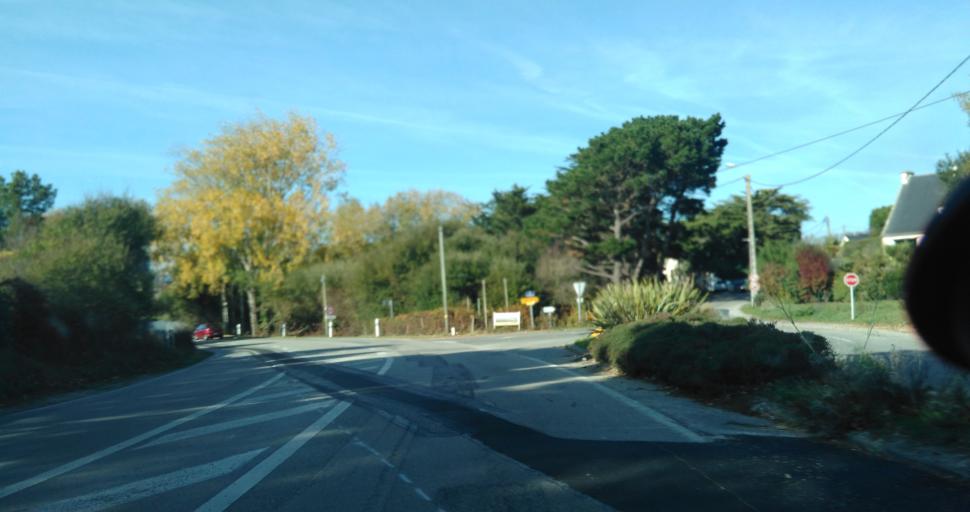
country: FR
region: Brittany
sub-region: Departement du Morbihan
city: Plouharnel
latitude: 47.5986
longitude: -3.1235
